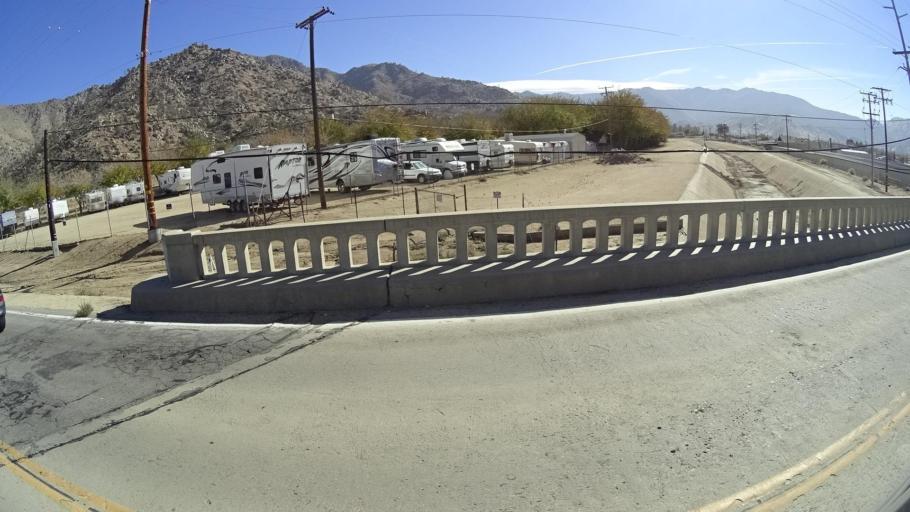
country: US
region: California
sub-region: Kern County
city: Lake Isabella
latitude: 35.6363
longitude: -118.4702
